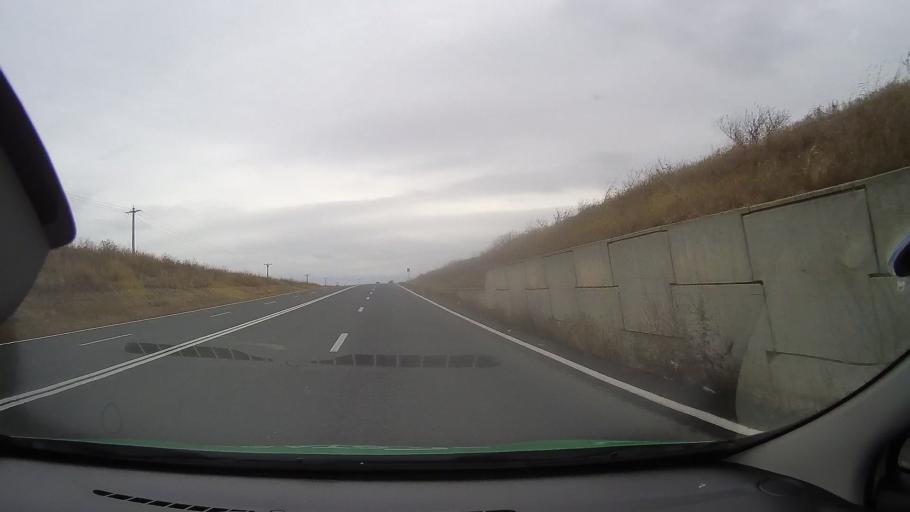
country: RO
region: Constanta
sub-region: Comuna Nicolae Balcescu
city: Nicolae Balcescu
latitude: 44.3807
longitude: 28.4069
